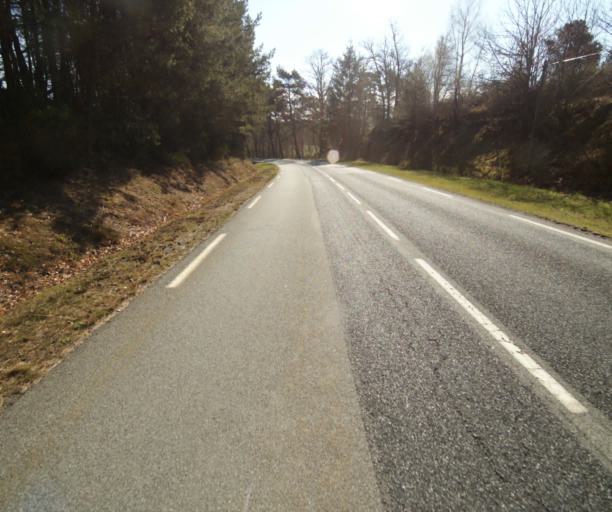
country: FR
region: Limousin
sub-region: Departement de la Correze
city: Correze
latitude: 45.2830
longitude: 1.9134
